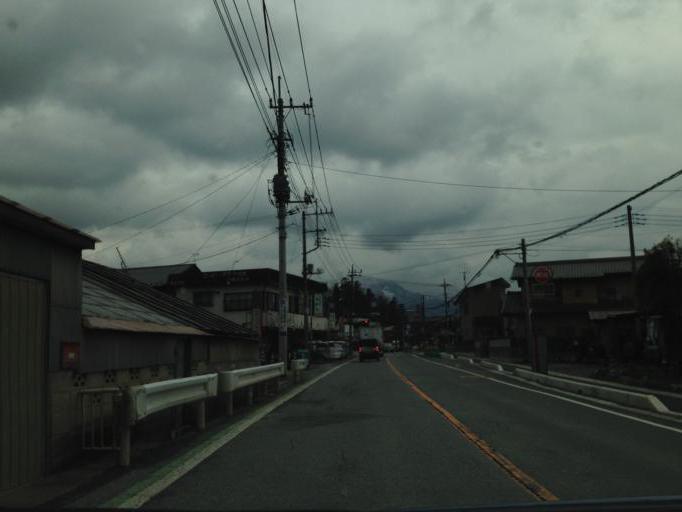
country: JP
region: Saitama
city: Chichibu
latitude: 36.0143
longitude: 139.0866
